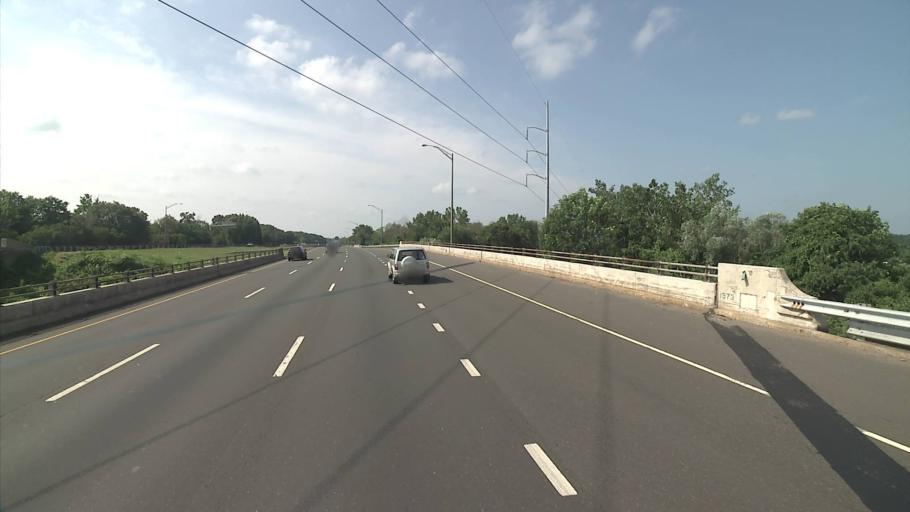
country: US
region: Connecticut
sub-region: New Haven County
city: North Haven
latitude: 41.3910
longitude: -72.8652
